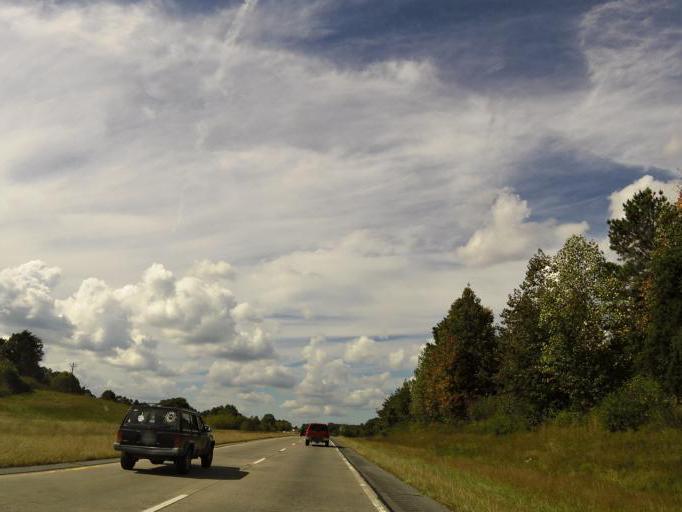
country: US
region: Georgia
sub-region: Pickens County
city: Jasper
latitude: 34.4488
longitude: -84.4473
